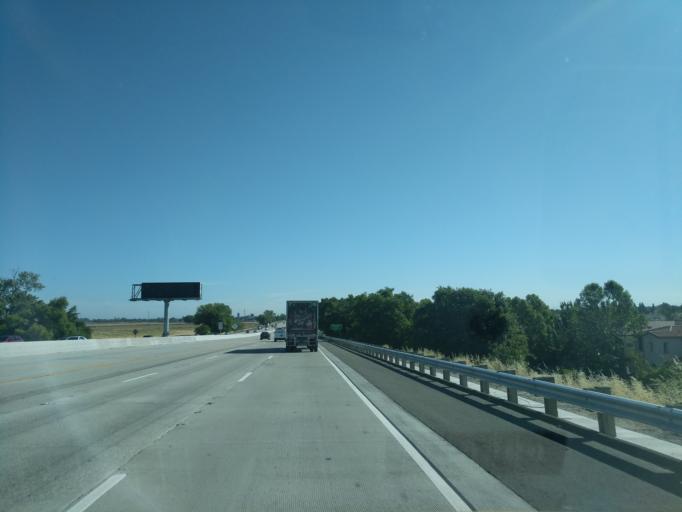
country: US
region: California
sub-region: Yolo County
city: West Sacramento
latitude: 38.6037
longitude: -121.5440
